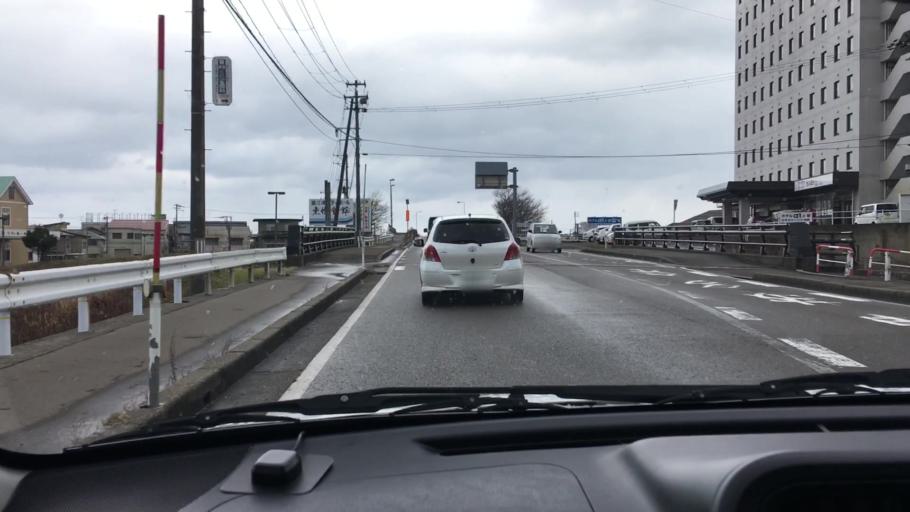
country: JP
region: Niigata
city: Joetsu
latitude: 37.1657
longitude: 138.2371
